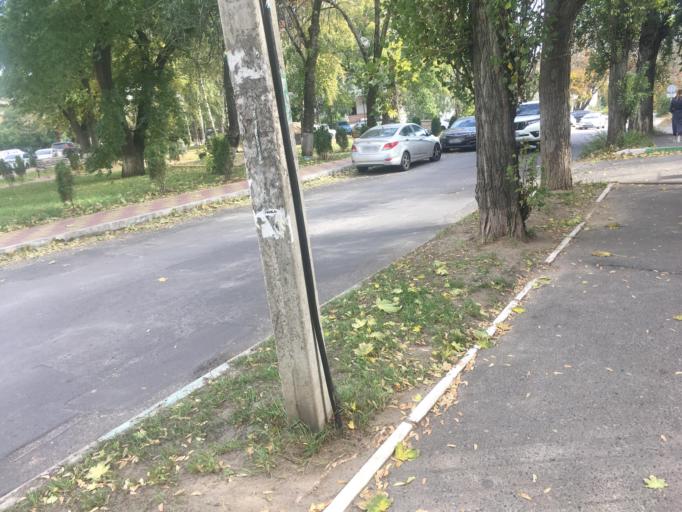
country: RU
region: Kursk
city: Kursk
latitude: 51.7456
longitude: 36.2007
